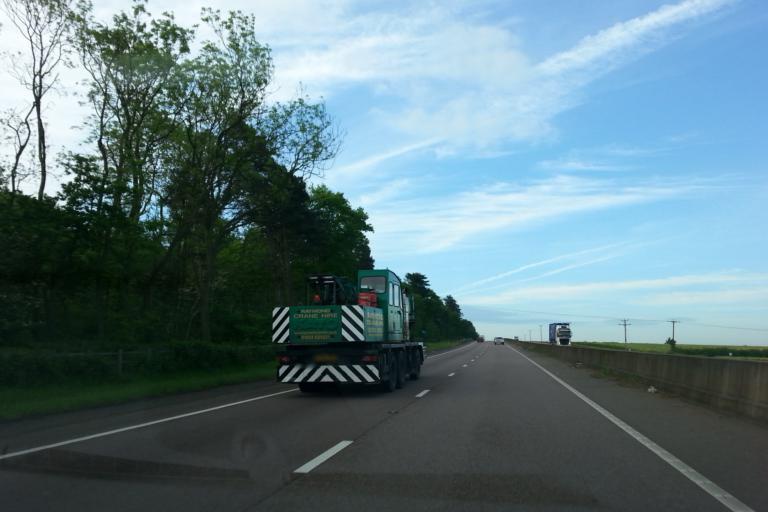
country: GB
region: England
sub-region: Nottinghamshire
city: Cotgrave
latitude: 52.8948
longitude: -1.0238
